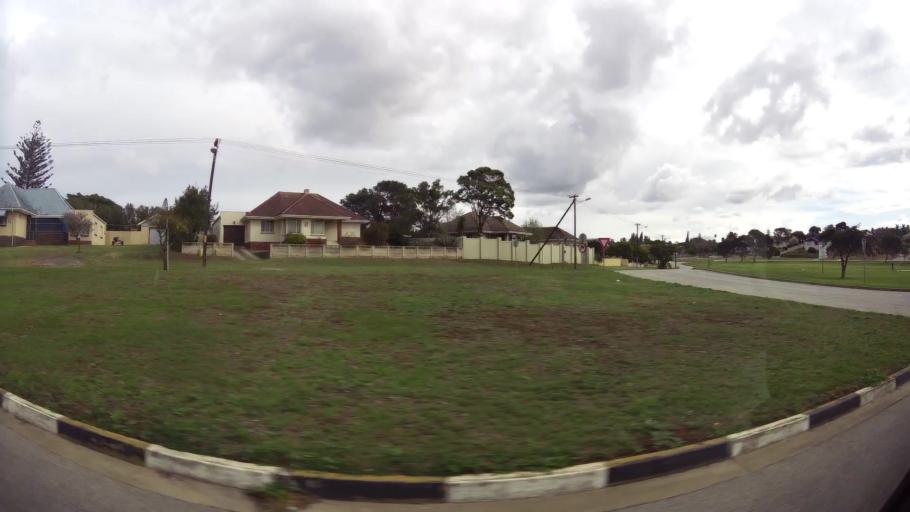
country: ZA
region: Eastern Cape
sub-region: Nelson Mandela Bay Metropolitan Municipality
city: Port Elizabeth
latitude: -33.9377
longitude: 25.5182
